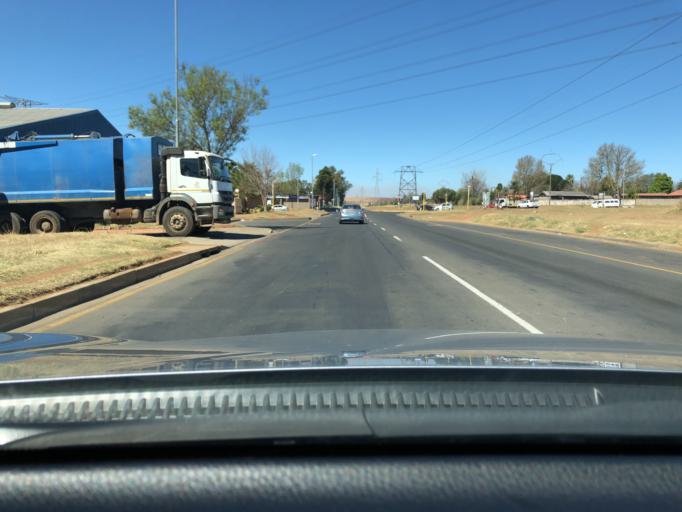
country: ZA
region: KwaZulu-Natal
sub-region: Amajuba District Municipality
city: Newcastle
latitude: -27.7619
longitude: 29.9531
